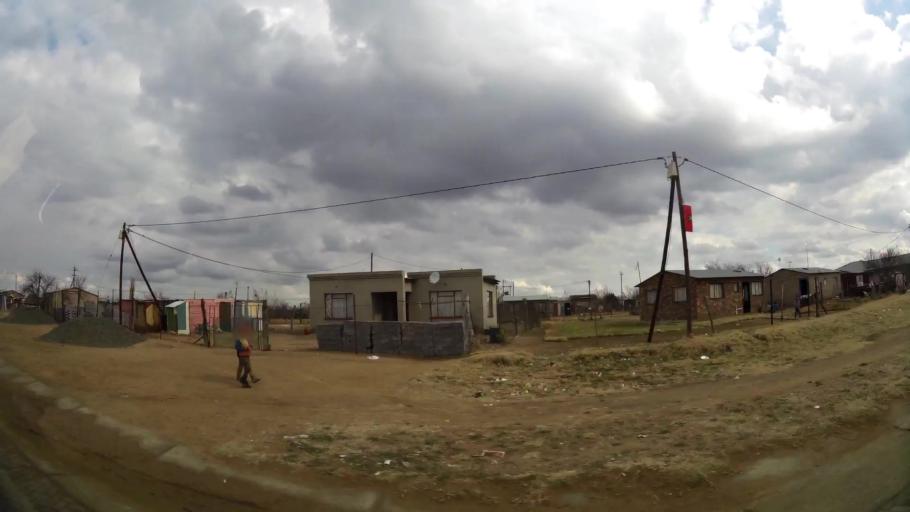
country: ZA
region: Orange Free State
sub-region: Fezile Dabi District Municipality
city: Sasolburg
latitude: -26.8795
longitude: 27.8801
